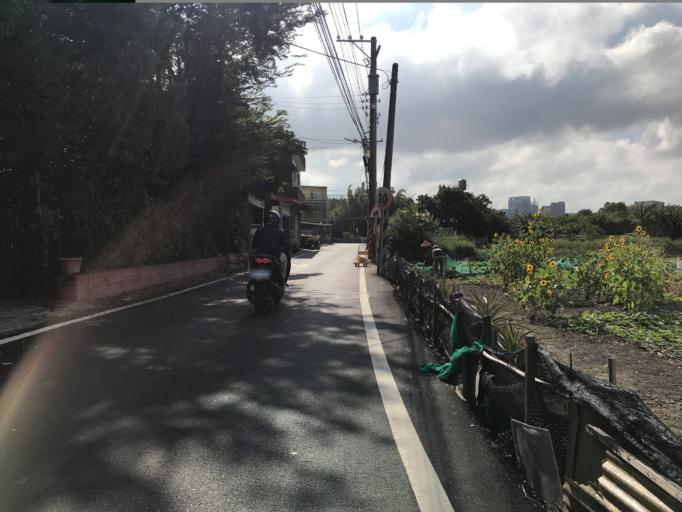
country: TW
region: Taiwan
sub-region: Hsinchu
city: Zhubei
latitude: 24.8112
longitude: 121.0021
